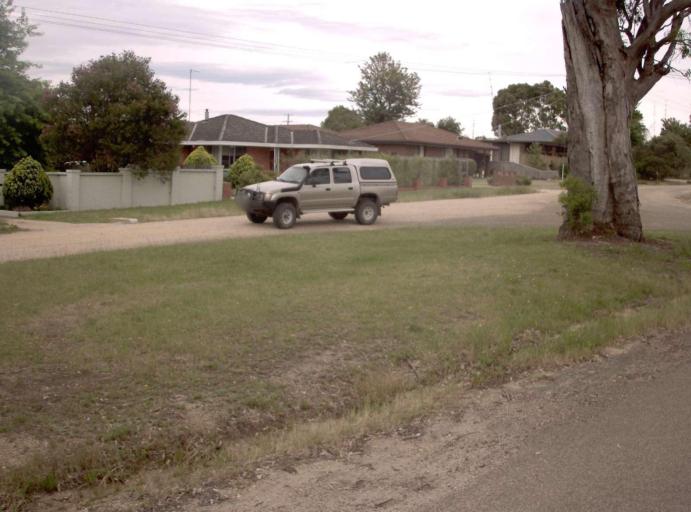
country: AU
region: Victoria
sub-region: East Gippsland
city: Bairnsdale
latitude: -37.8035
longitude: 147.6158
